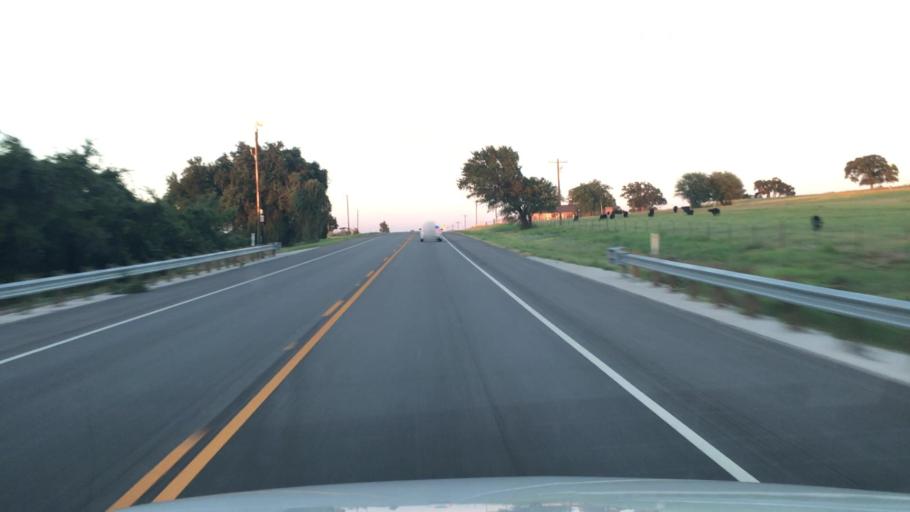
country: US
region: Texas
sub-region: Somervell County
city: Glen Rose
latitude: 32.1903
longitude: -97.8555
